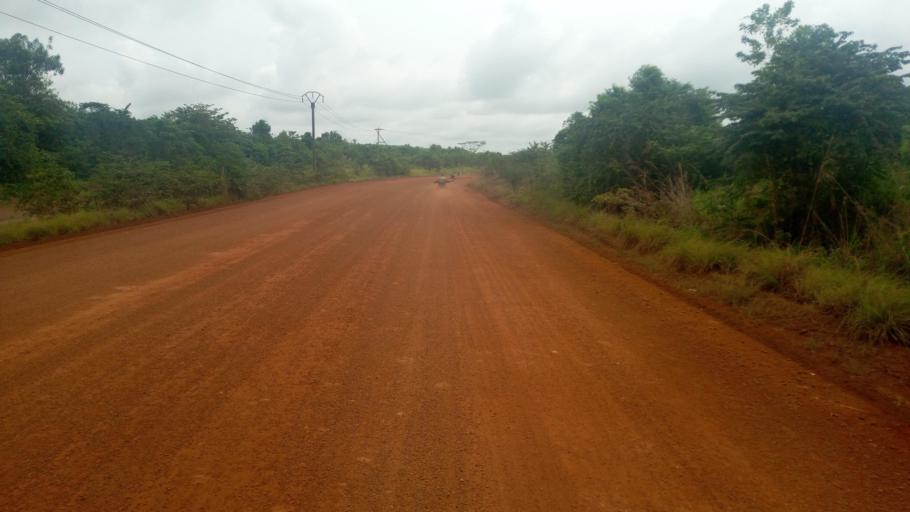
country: SL
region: Southern Province
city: Mogbwemo
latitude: 7.7197
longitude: -12.2856
